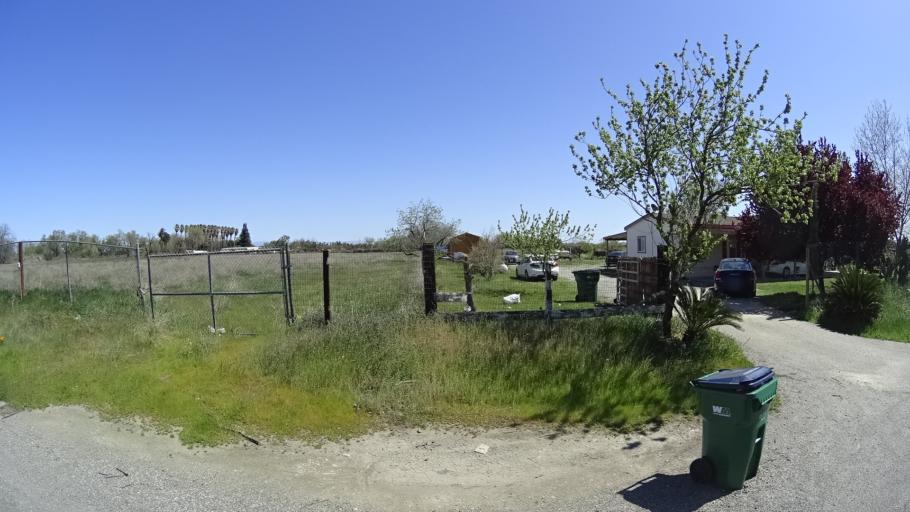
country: US
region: California
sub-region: Glenn County
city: Orland
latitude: 39.7703
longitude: -122.2476
